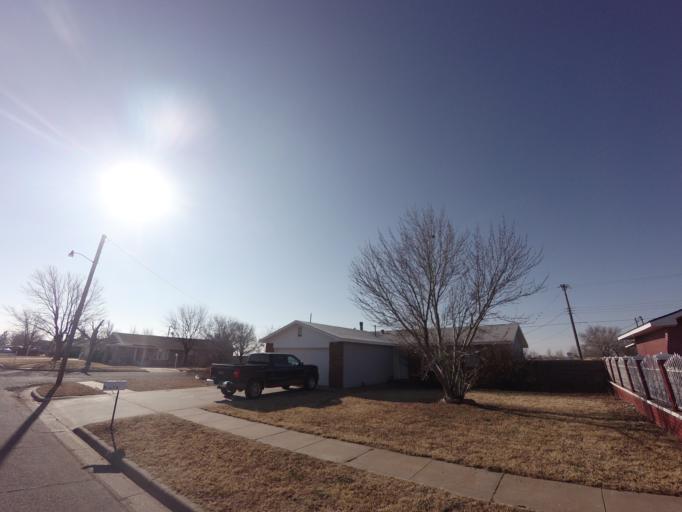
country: US
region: New Mexico
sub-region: Curry County
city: Clovis
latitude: 34.3809
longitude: -103.1926
